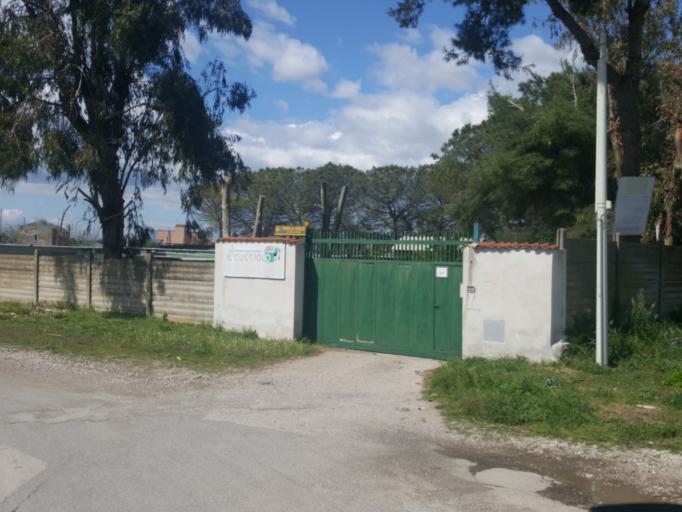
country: IT
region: Campania
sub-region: Provincia di Napoli
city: Torretta-Scalzapecora
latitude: 40.9357
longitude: 14.1044
